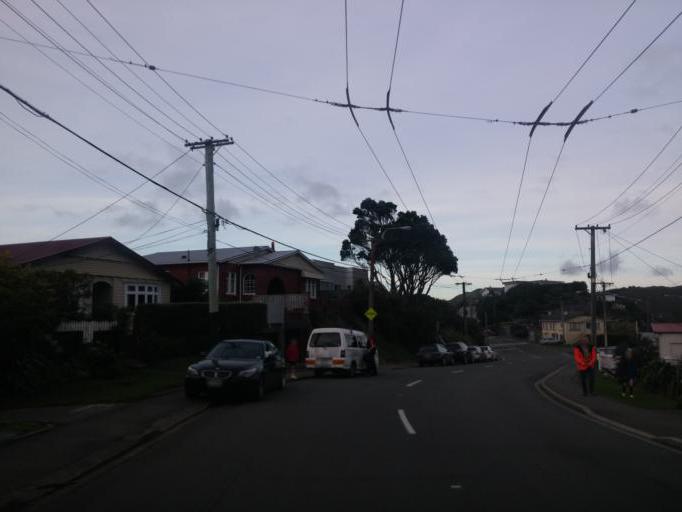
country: NZ
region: Wellington
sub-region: Wellington City
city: Brooklyn
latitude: -41.3171
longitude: 174.7649
